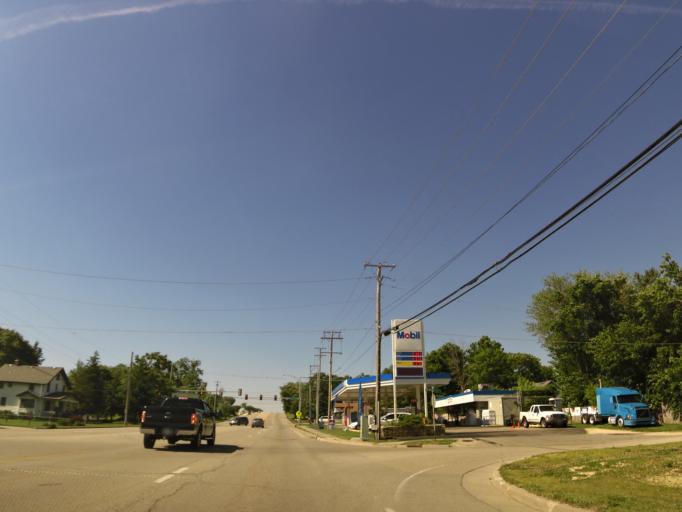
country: US
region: Illinois
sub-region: Ogle County
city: Davis Junction
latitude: 42.1862
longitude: -89.0720
